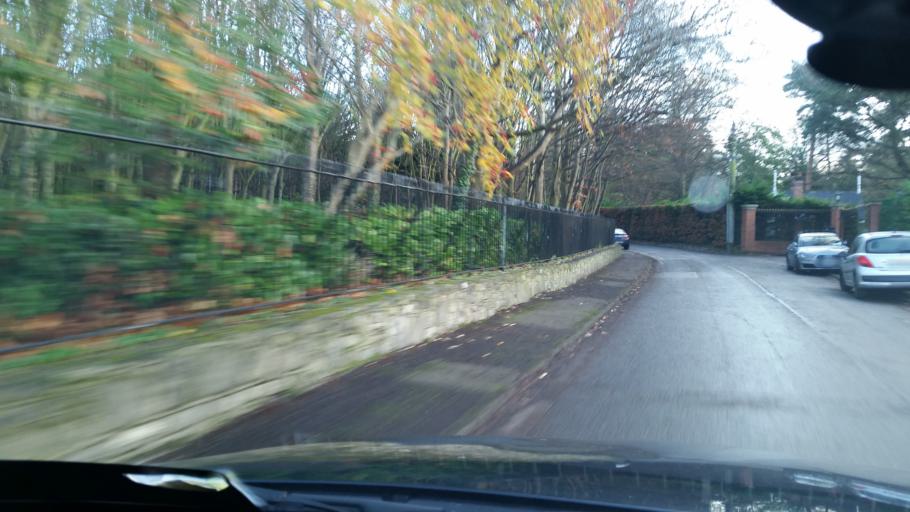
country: IE
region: Leinster
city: Glasnevin
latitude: 53.3812
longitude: -6.2629
